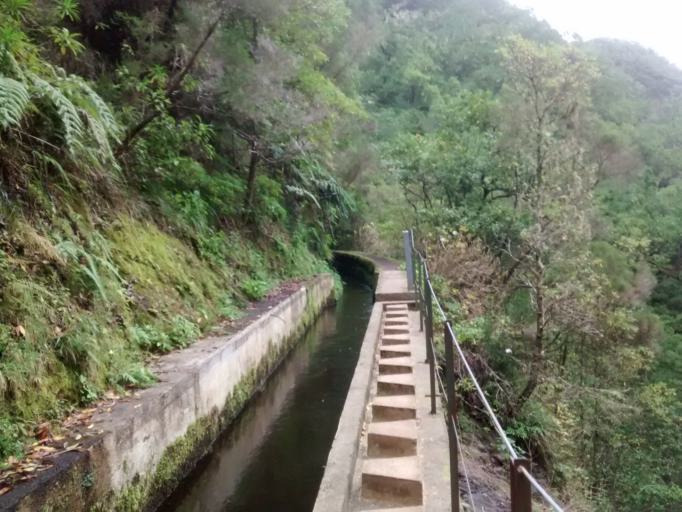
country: PT
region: Madeira
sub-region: Sao Vicente
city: Sao Vicente
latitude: 32.7519
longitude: -17.0402
